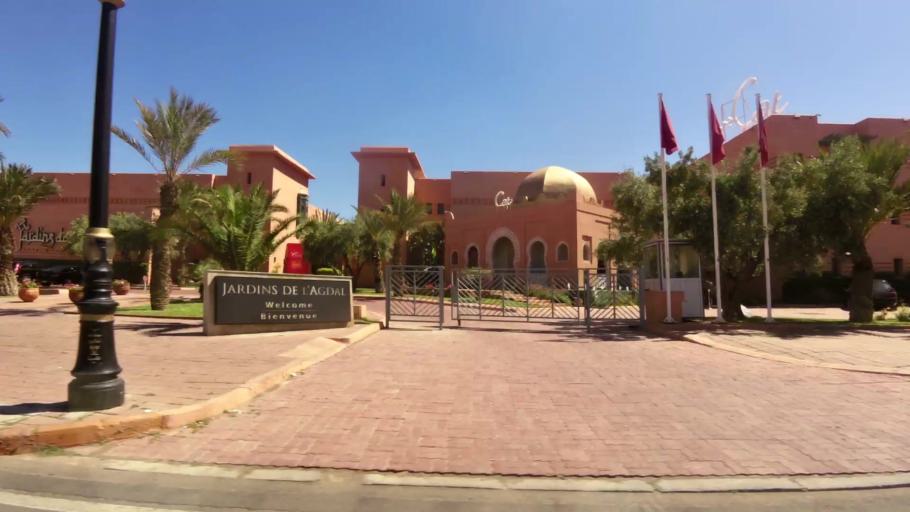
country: MA
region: Marrakech-Tensift-Al Haouz
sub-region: Marrakech
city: Marrakesh
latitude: 31.5937
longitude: -7.9921
